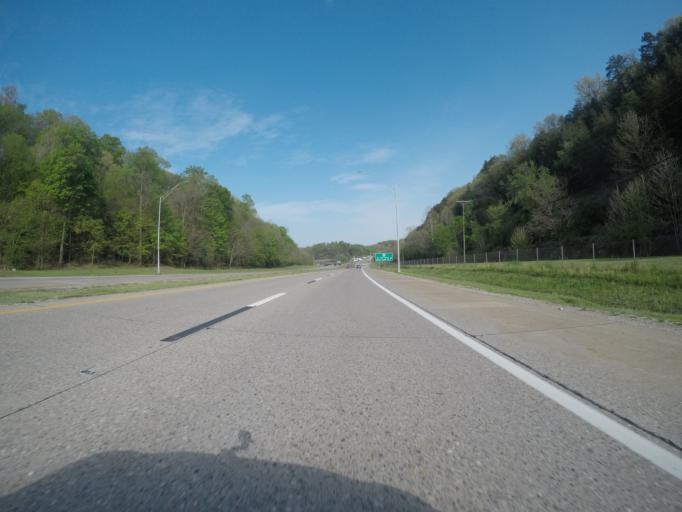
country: US
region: West Virginia
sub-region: Kanawha County
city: South Charleston
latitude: 38.3390
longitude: -81.6957
